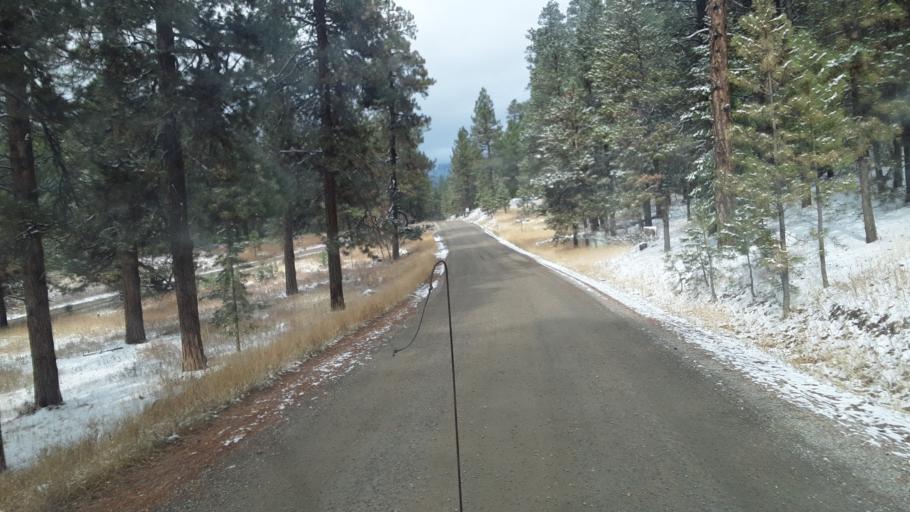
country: US
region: Colorado
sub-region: La Plata County
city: Bayfield
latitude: 37.4082
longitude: -107.5347
